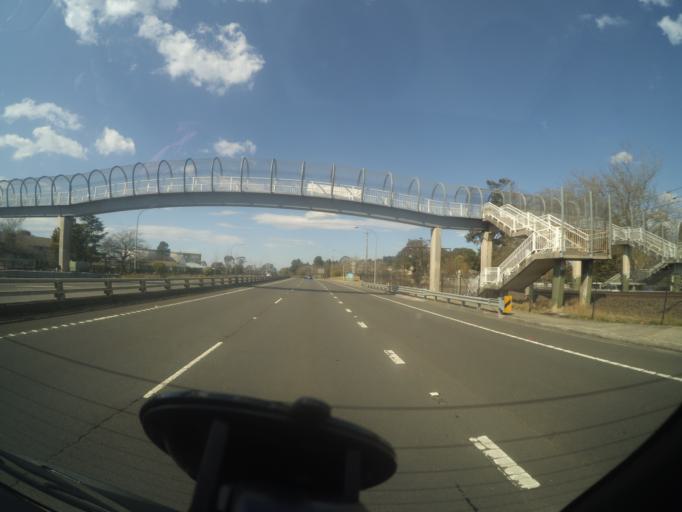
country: AU
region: New South Wales
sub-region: Blue Mountains Municipality
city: Leura
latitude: -33.7119
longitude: 150.3356
